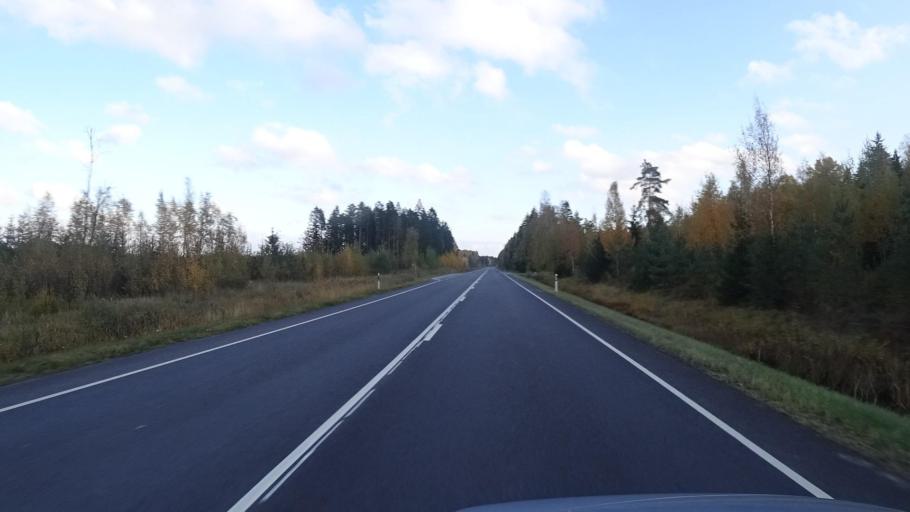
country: FI
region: Satakunta
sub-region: Rauma
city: Koeylioe
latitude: 61.0878
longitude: 22.2541
